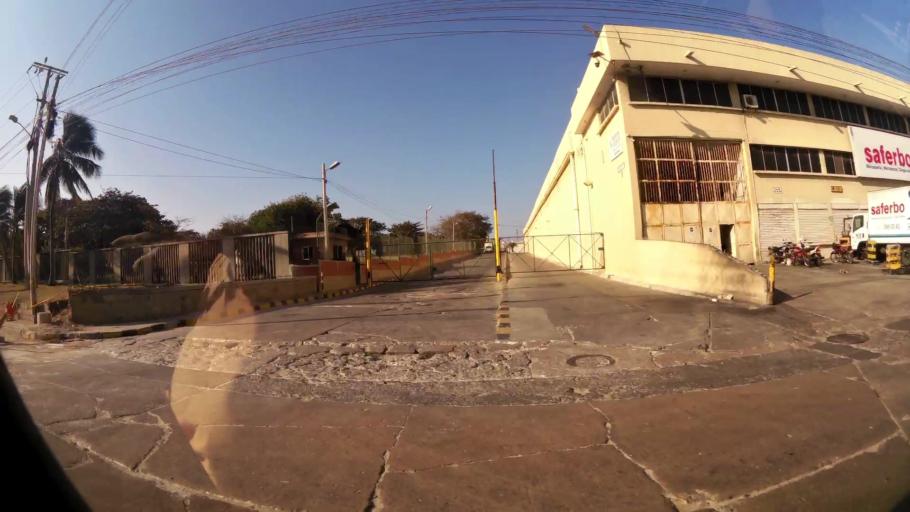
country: CO
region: Atlantico
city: Barranquilla
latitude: 11.0293
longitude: -74.8065
